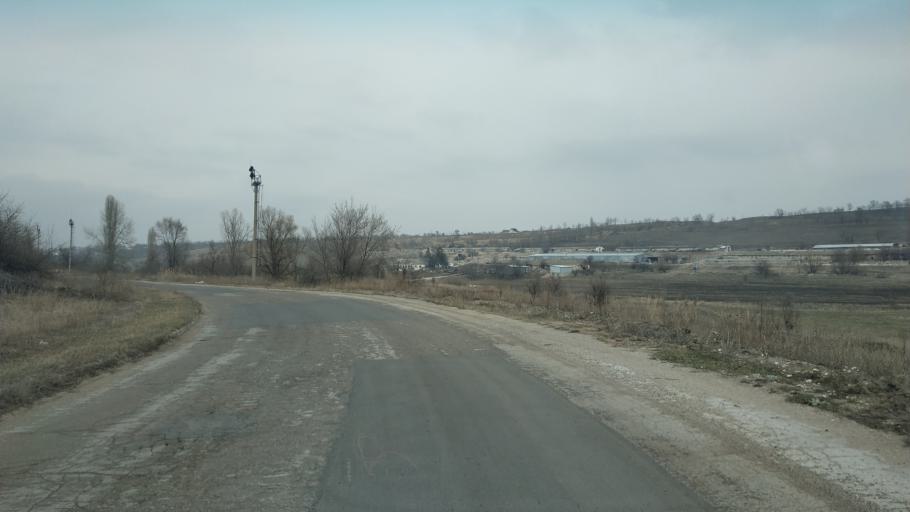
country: MD
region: Chisinau
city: Singera
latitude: 46.8977
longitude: 29.0219
